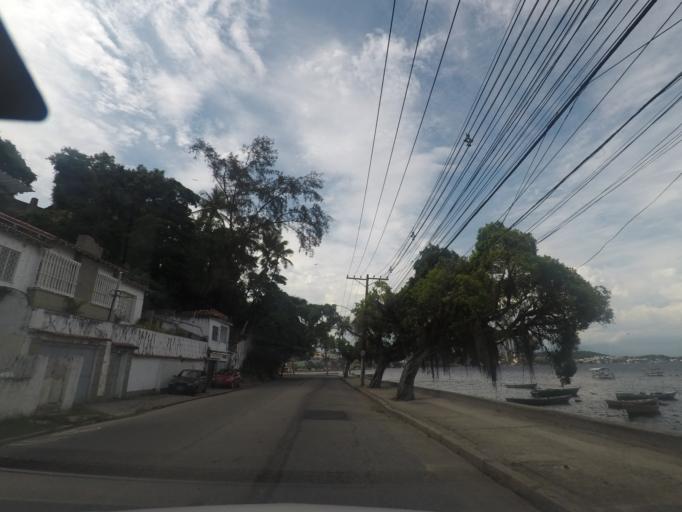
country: BR
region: Rio de Janeiro
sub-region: Rio De Janeiro
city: Rio de Janeiro
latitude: -22.8118
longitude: -43.1765
